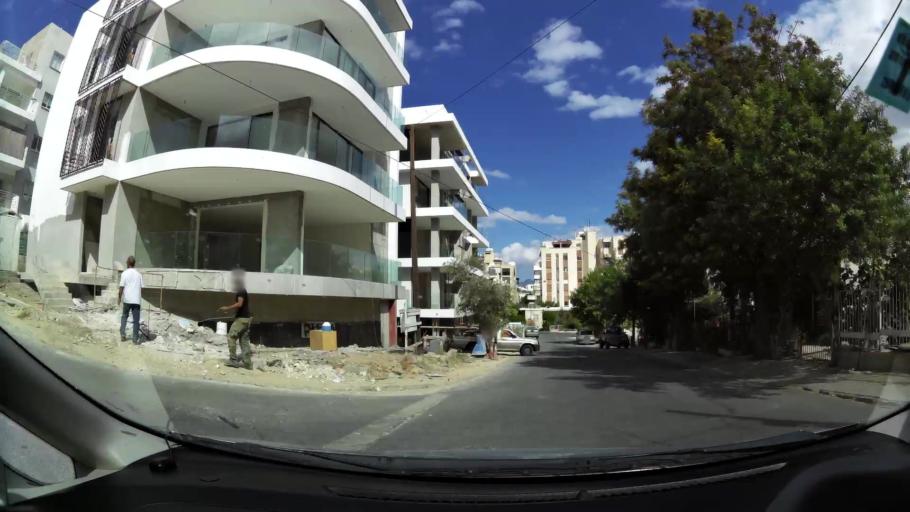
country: CY
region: Lefkosia
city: Nicosia
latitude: 35.1539
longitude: 33.3722
